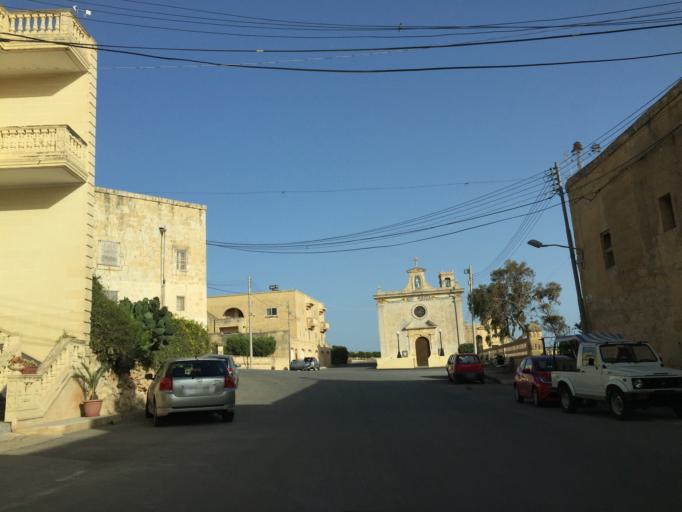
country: MT
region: Il-Qala
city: Qala
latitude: 36.0347
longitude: 14.3204
